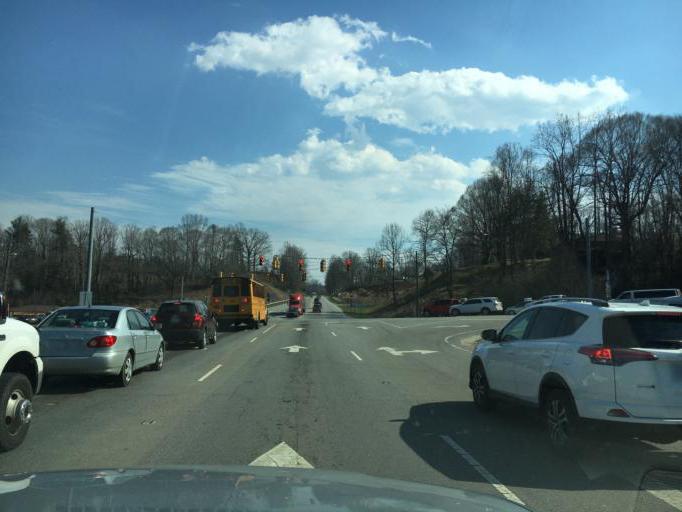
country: US
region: North Carolina
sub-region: McDowell County
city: Marion
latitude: 35.6645
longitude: -81.9786
